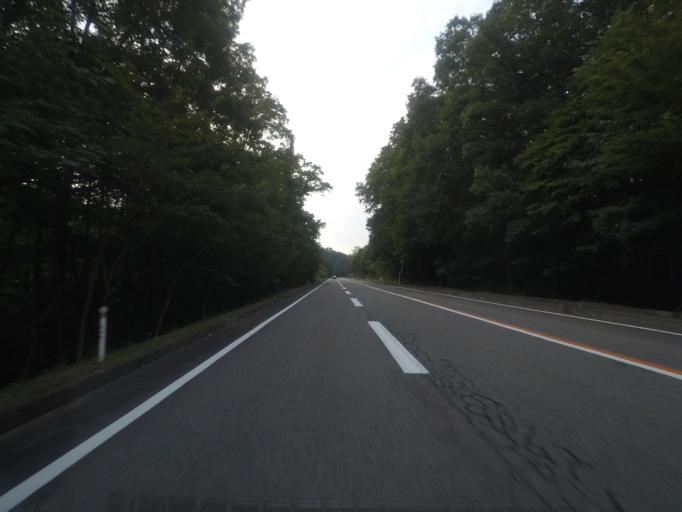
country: JP
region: Fukushima
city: Funehikimachi-funehiki
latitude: 37.5755
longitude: 140.7279
